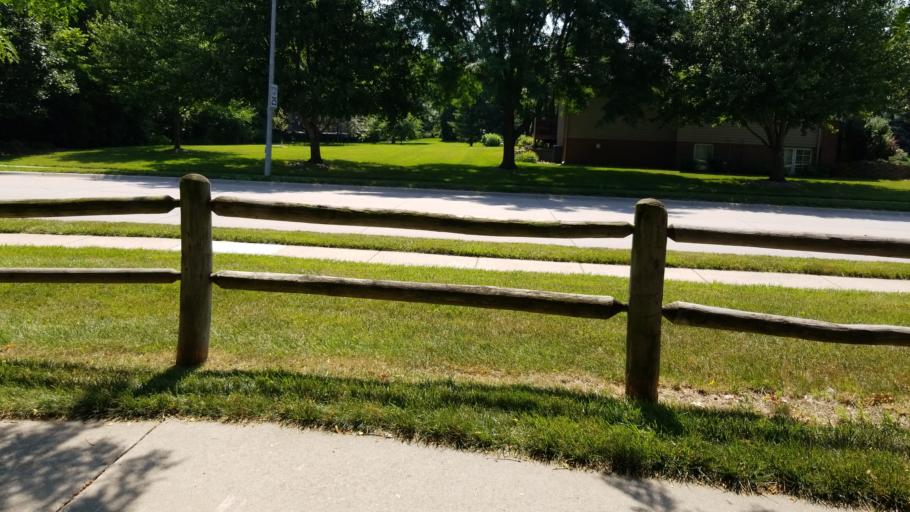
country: US
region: Nebraska
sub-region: Douglas County
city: Elkhorn
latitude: 41.2794
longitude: -96.1645
